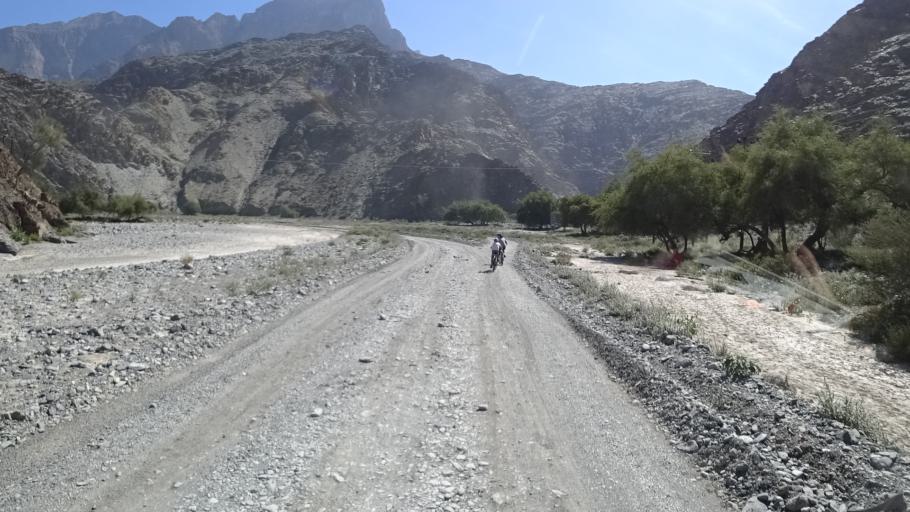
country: OM
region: Al Batinah
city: Bayt al `Awabi
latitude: 23.2586
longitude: 57.4397
